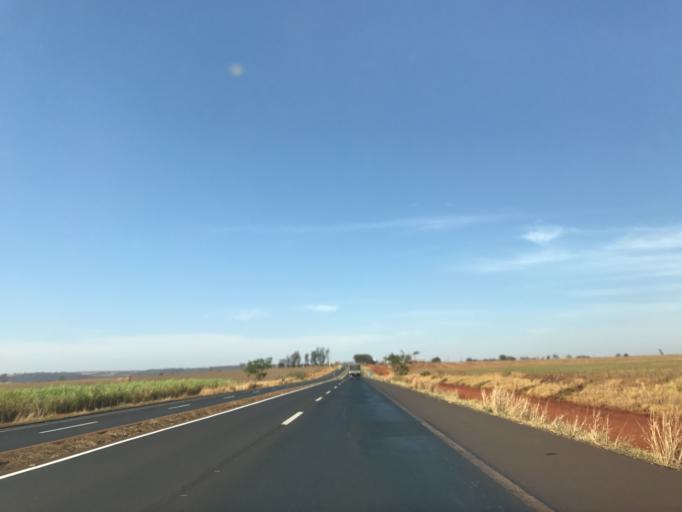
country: BR
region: Minas Gerais
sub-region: Centralina
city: Centralina
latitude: -18.5576
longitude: -49.1938
